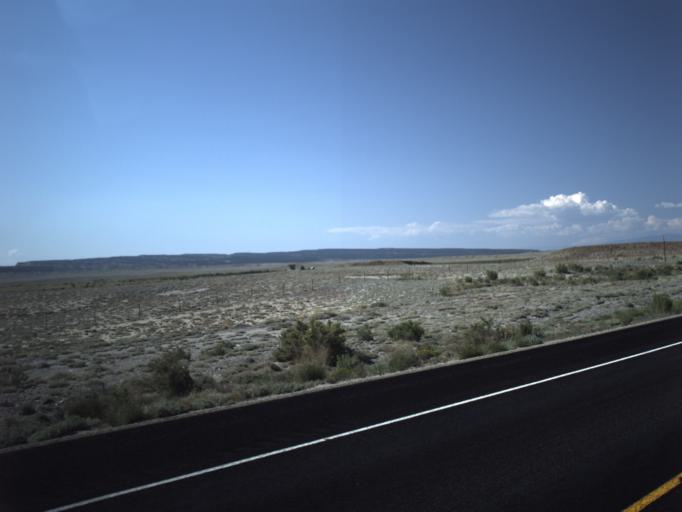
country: US
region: Utah
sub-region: Emery County
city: Ferron
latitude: 39.0245
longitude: -111.1350
